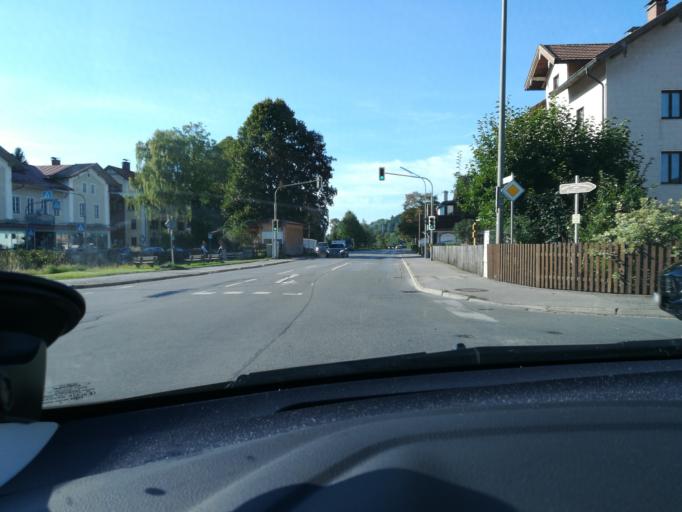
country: DE
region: Bavaria
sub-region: Upper Bavaria
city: Hausham
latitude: 47.7475
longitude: 11.8427
